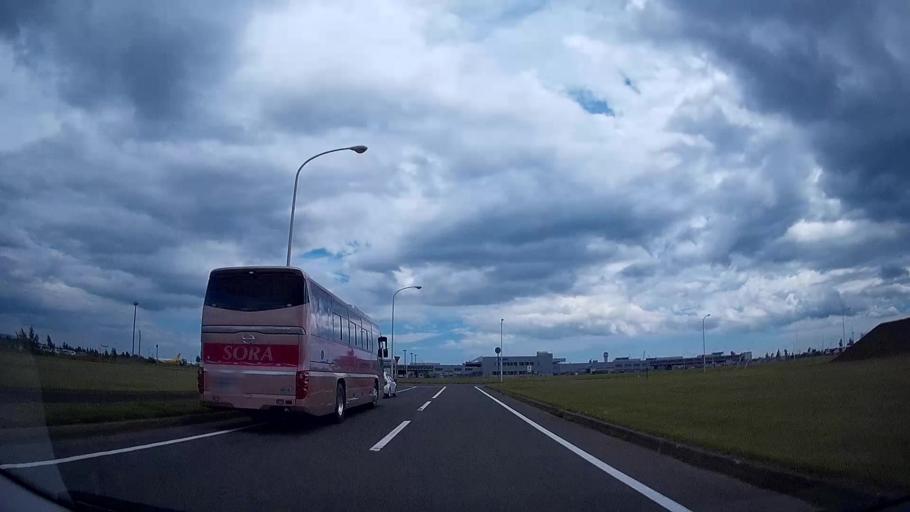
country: JP
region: Hokkaido
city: Chitose
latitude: 42.7982
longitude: 141.6803
